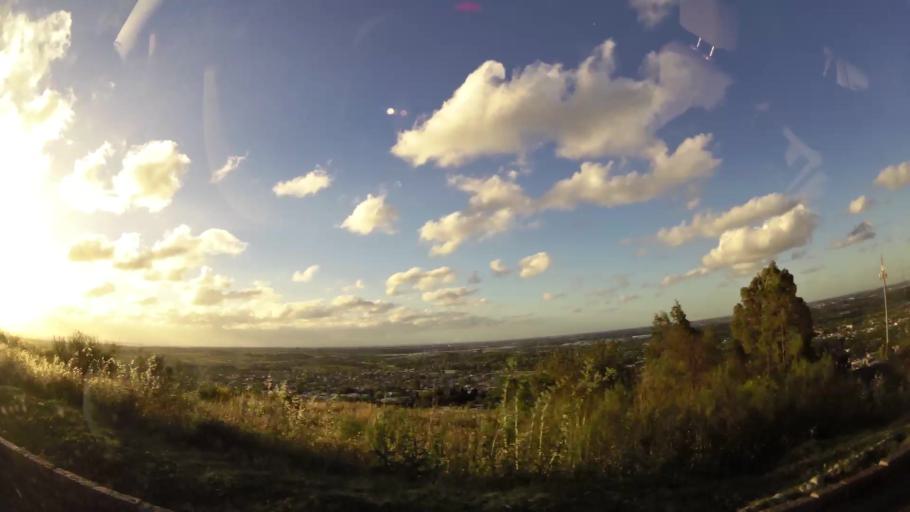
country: UY
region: Montevideo
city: Montevideo
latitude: -34.8879
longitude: -56.2606
